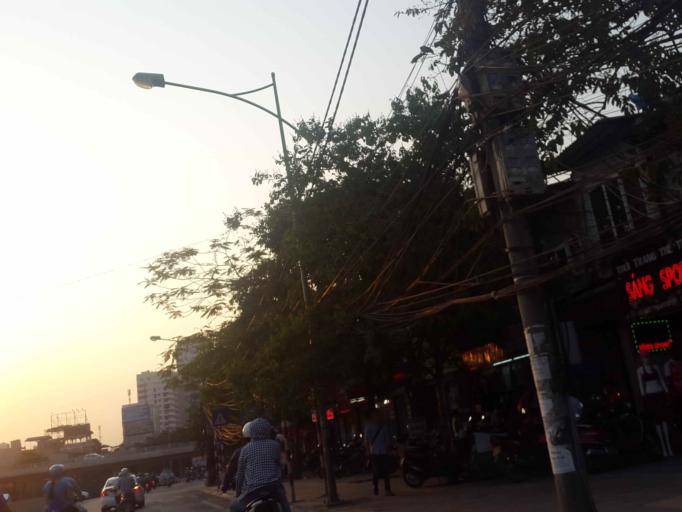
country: VN
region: Ha Noi
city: Cau Giay
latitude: 21.0295
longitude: 105.8033
